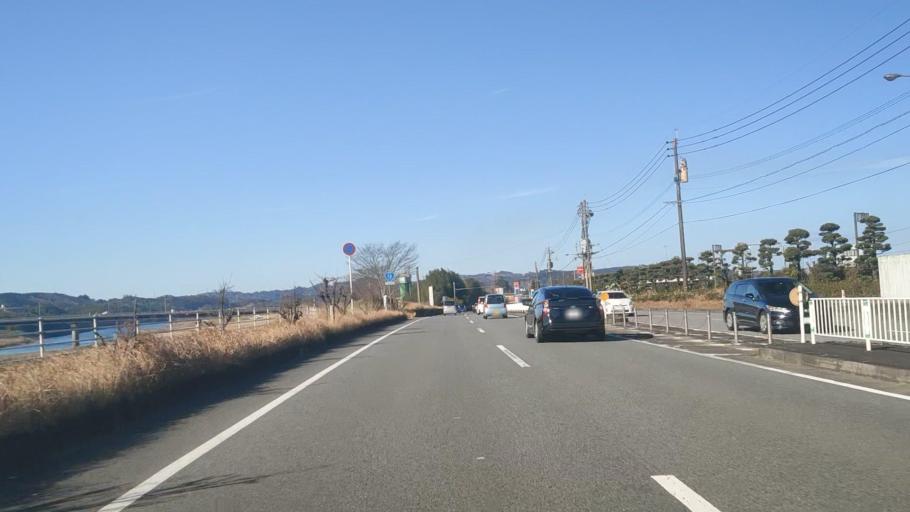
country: JP
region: Oita
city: Oita
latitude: 33.1378
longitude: 131.6588
